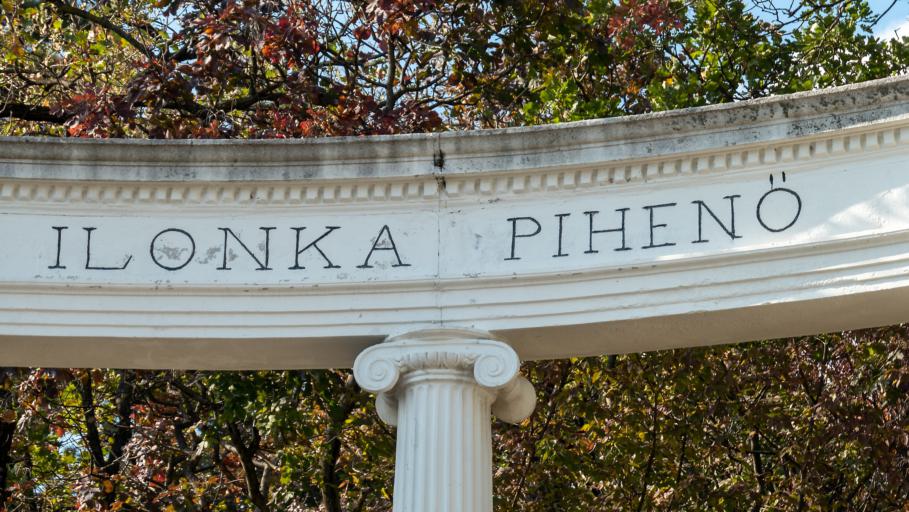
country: HU
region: Baranya
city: Pecs
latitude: 46.0895
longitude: 18.2314
